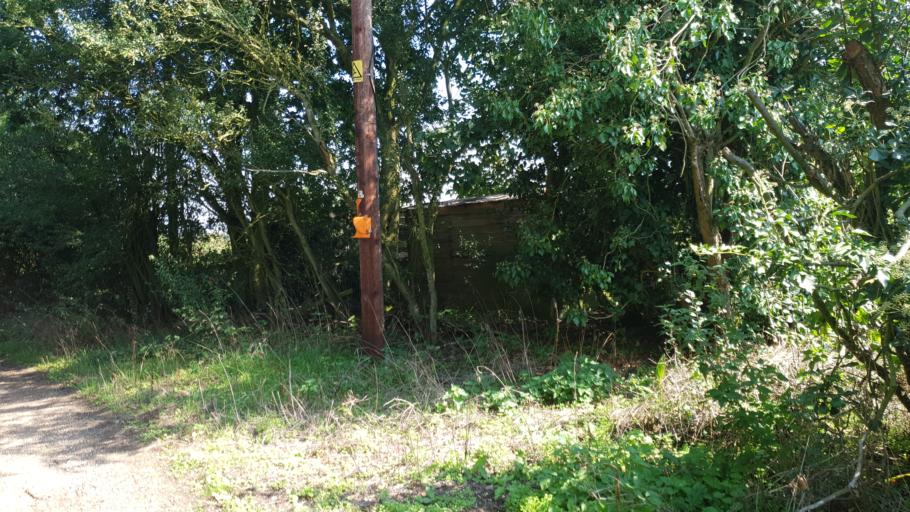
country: GB
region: England
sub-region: Essex
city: Wivenhoe
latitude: 51.9214
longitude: 0.9781
